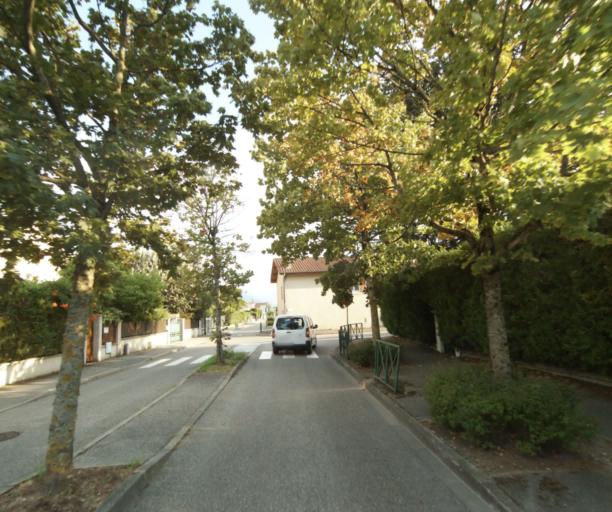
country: FR
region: Rhone-Alpes
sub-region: Departement de l'Isere
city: Seyssinet-Pariset
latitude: 45.1654
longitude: 5.6966
